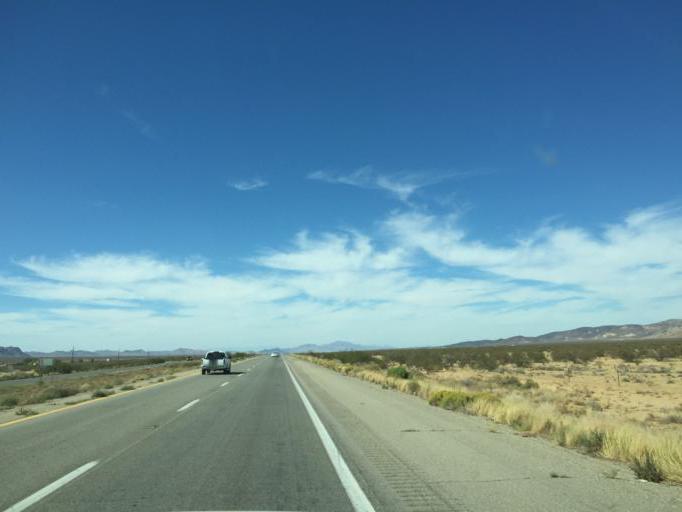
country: US
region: Arizona
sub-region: Mohave County
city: Dolan Springs
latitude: 35.5643
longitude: -114.3762
